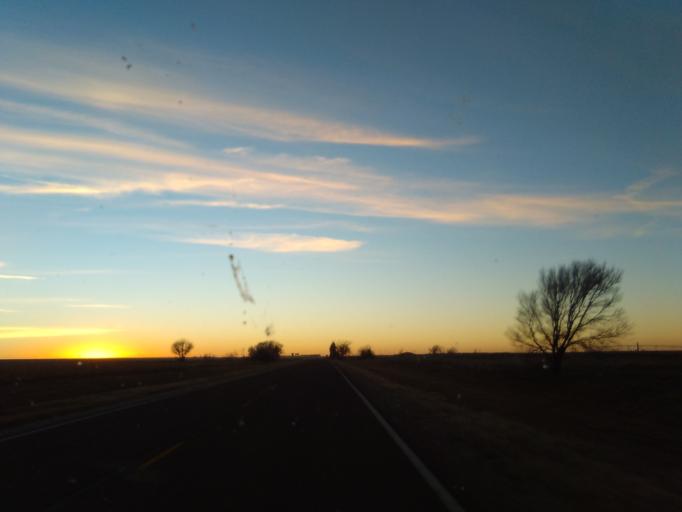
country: US
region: Kansas
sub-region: Wallace County
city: Sharon Springs
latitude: 38.8582
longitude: -102.0415
